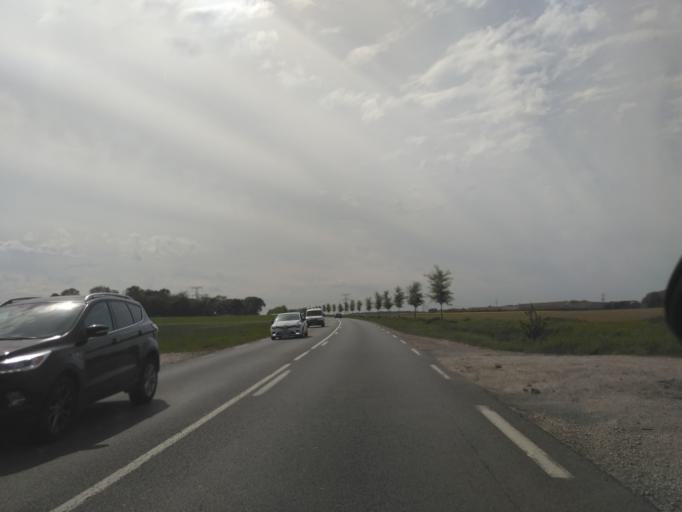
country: FR
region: Ile-de-France
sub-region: Departement de Seine-et-Marne
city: Ozouer-le-Voulgis
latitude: 48.6362
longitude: 2.7621
